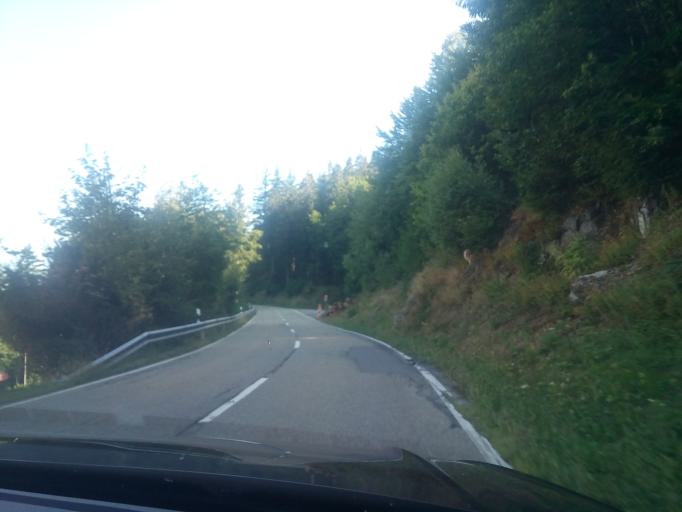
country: DE
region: Baden-Wuerttemberg
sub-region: Karlsruhe Region
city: Buhlertal
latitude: 48.6599
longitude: 8.2205
